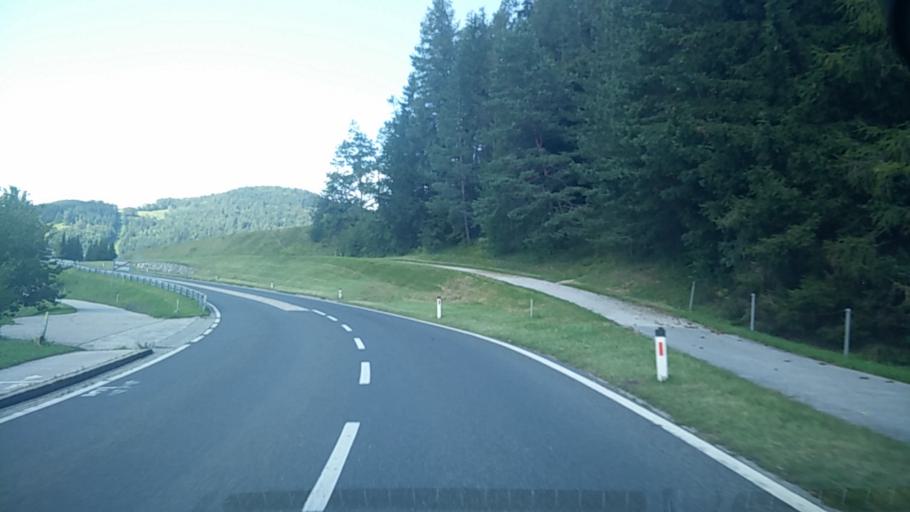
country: AT
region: Carinthia
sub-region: Politischer Bezirk Volkermarkt
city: Sittersdorf
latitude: 46.5381
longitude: 14.5980
